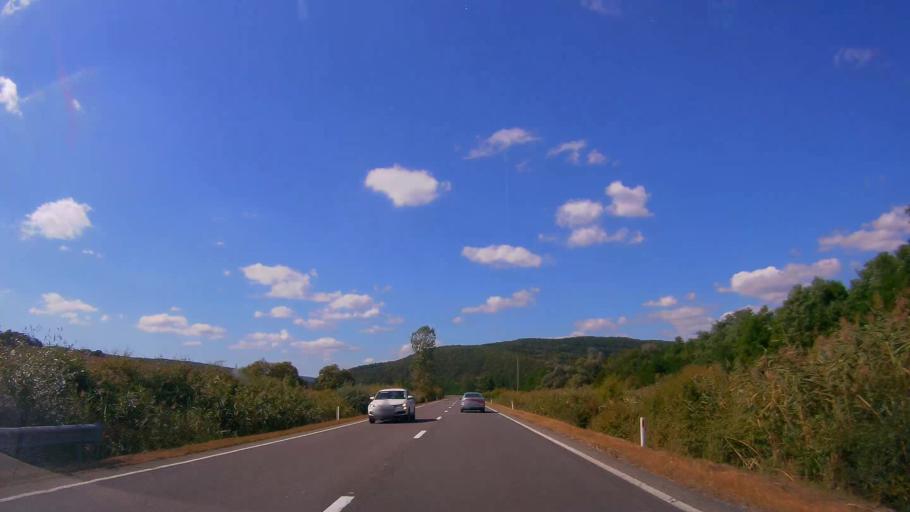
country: RO
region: Salaj
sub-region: Comuna Sanmihaiu Almasului
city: Sanmihaiu Almasului
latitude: 46.9638
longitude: 23.3133
